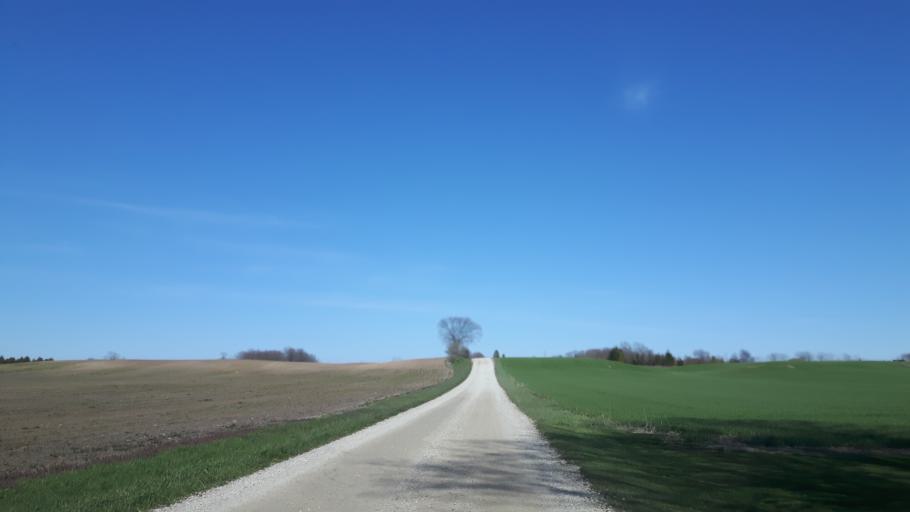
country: CA
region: Ontario
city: Goderich
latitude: 43.6613
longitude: -81.6833
